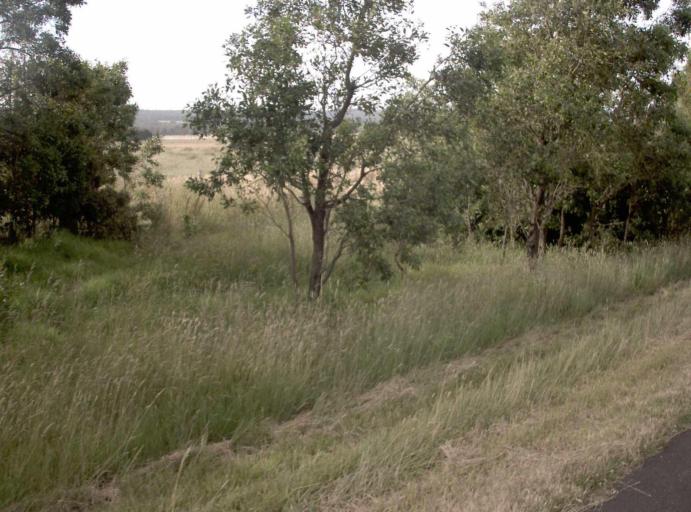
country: AU
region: Victoria
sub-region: Latrobe
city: Traralgon
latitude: -38.0862
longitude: 146.6044
